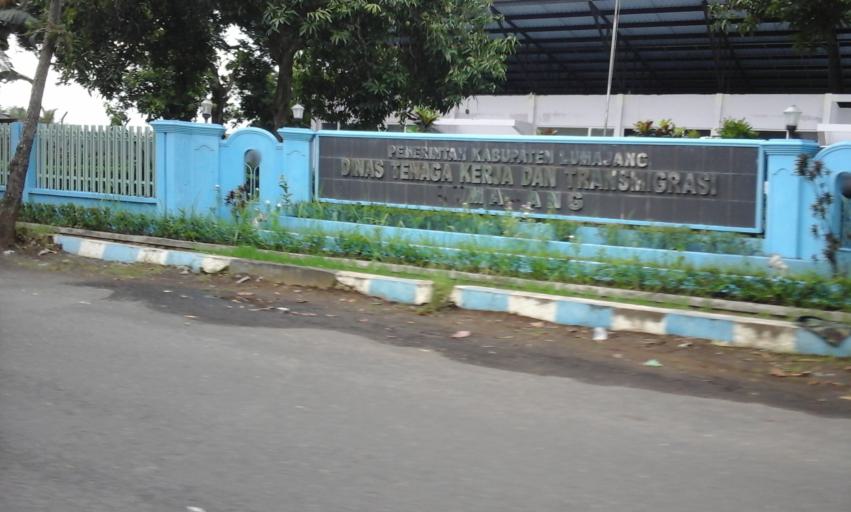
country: ID
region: East Java
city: Rogotrunan
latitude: -8.1191
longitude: 113.2235
